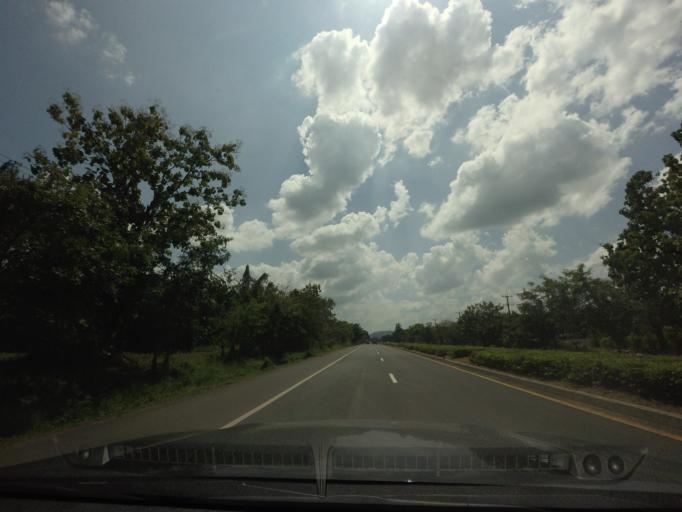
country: TH
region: Phetchabun
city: Phetchabun
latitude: 16.2768
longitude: 101.0597
